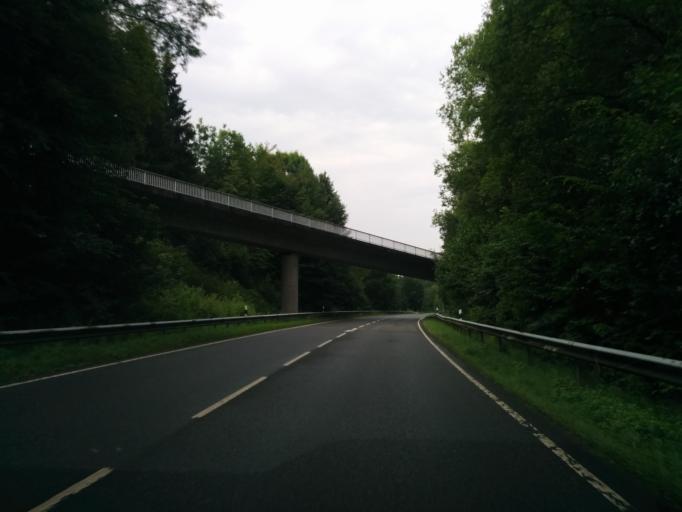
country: DE
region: Lower Saxony
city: Ebergotzen
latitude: 51.5694
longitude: 10.0971
